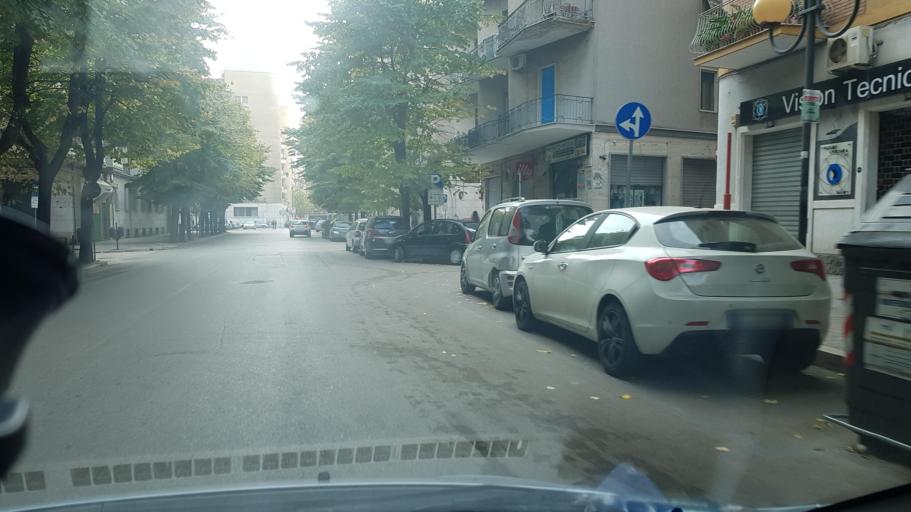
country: IT
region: Apulia
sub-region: Provincia di Foggia
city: Foggia
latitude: 41.4642
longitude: 15.5481
